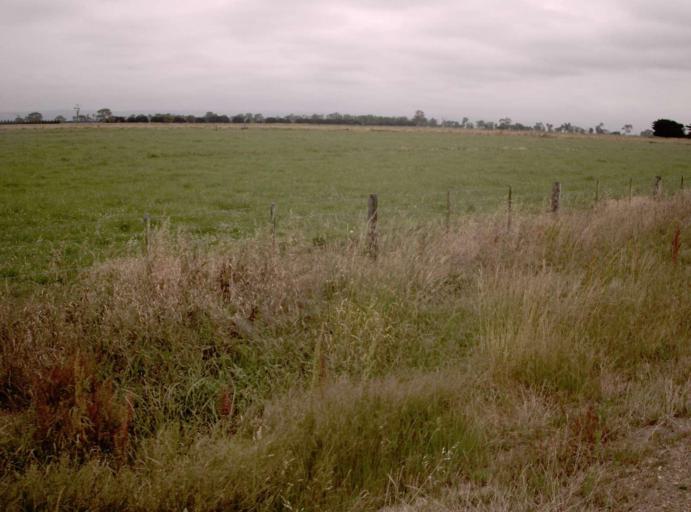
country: AU
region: Victoria
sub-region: Wellington
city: Heyfield
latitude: -38.0680
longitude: 146.7699
